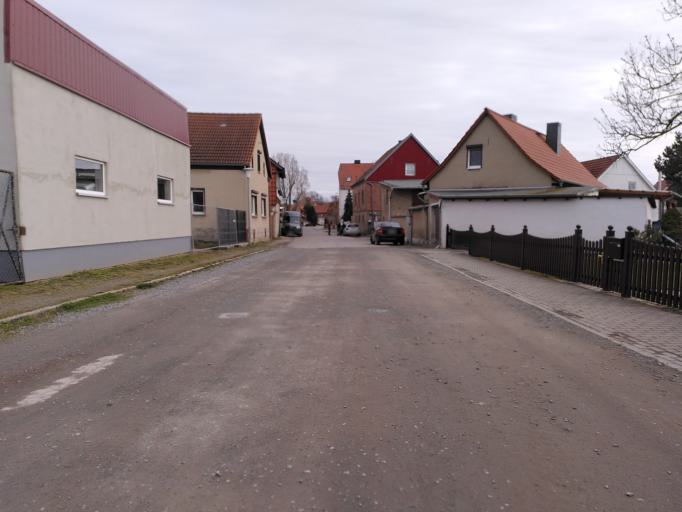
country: DE
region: Saxony-Anhalt
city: Ballenstedt
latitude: 51.7671
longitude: 11.2392
